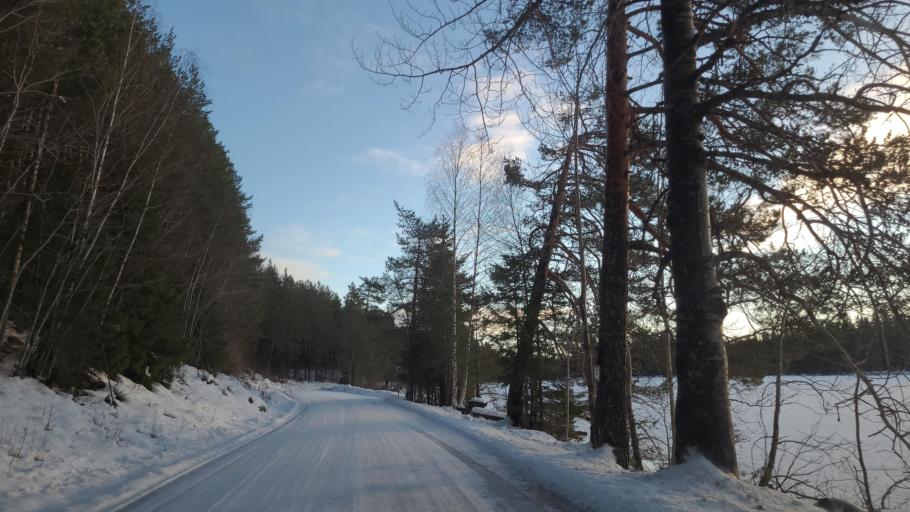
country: SE
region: Gaevleborg
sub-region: Bollnas Kommun
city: Kilafors
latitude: 61.3888
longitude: 16.6866
